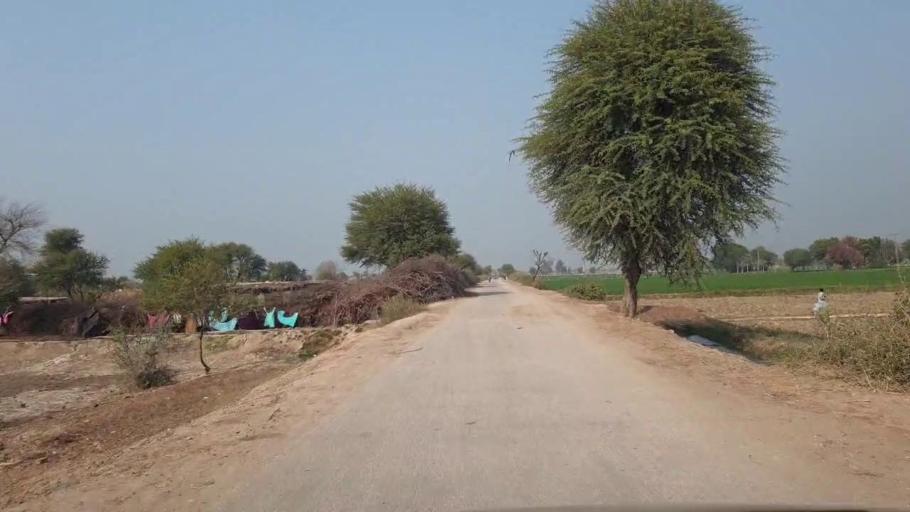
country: PK
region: Sindh
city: Hala
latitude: 25.8515
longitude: 68.4619
